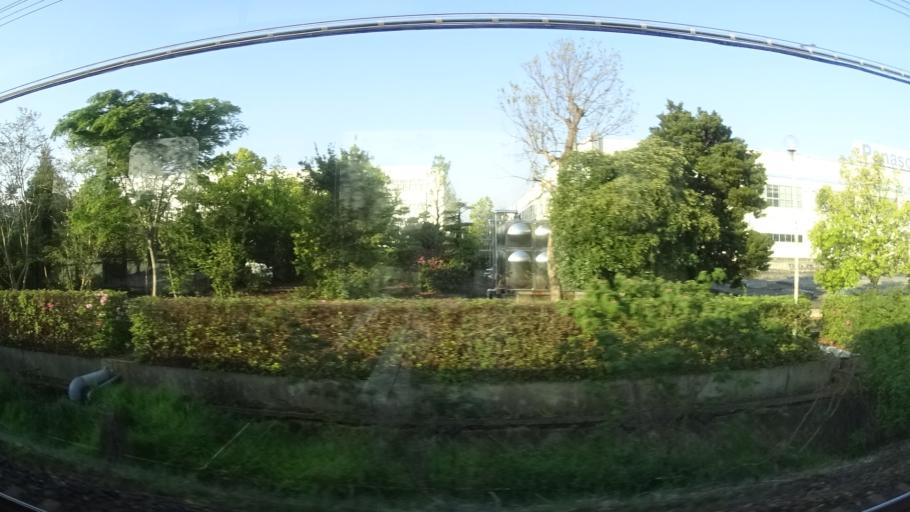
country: JP
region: Mie
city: Hisai-motomachi
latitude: 34.5584
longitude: 136.5611
